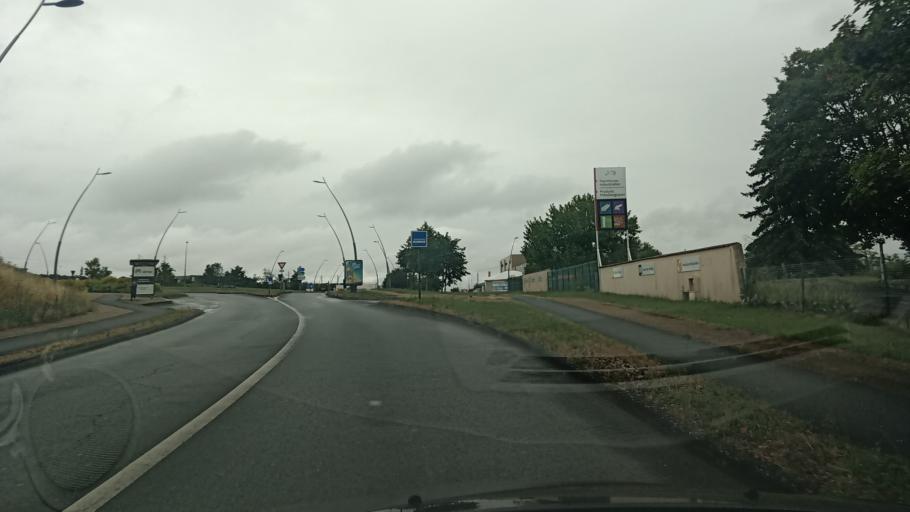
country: FR
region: Poitou-Charentes
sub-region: Departement de la Vienne
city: Poitiers
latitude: 46.6115
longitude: 0.3487
